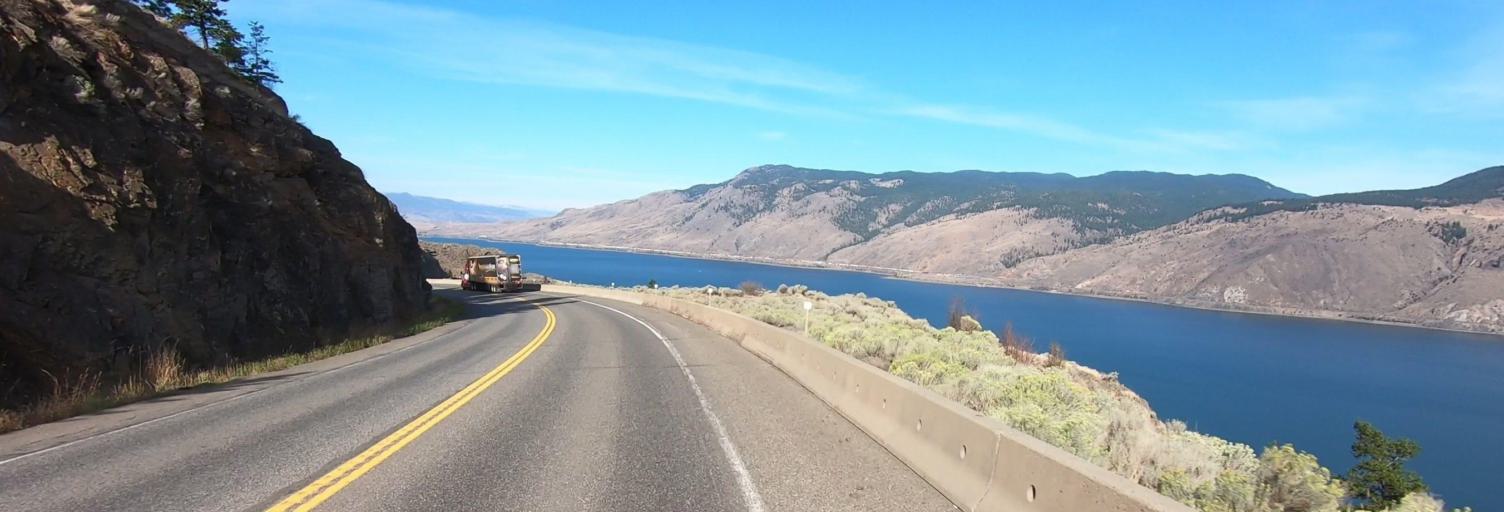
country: CA
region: British Columbia
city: Logan Lake
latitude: 50.7661
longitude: -120.7634
